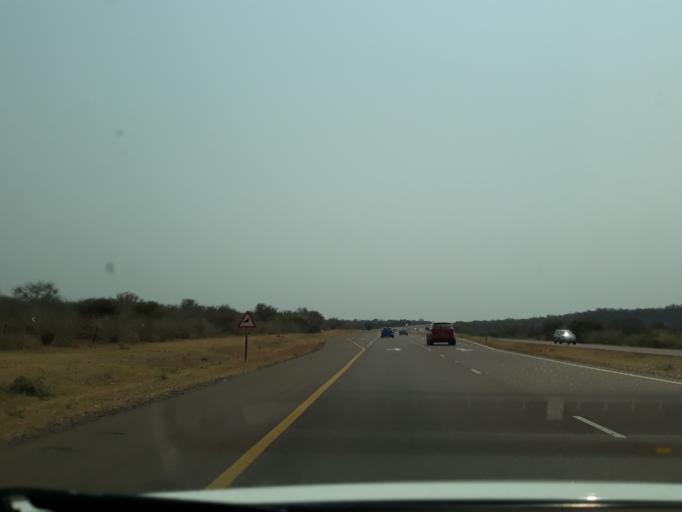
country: BW
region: Kgatleng
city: Bokaa
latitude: -24.4271
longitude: 26.0472
